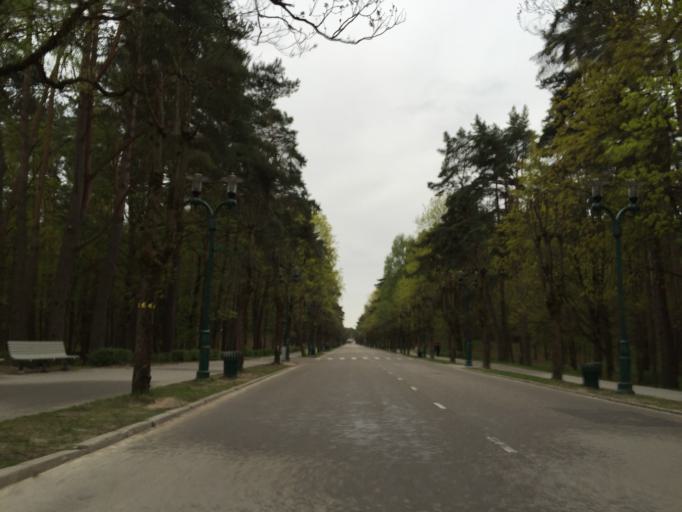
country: LV
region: Riga
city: Jaunciems
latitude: 57.0112
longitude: 24.1562
